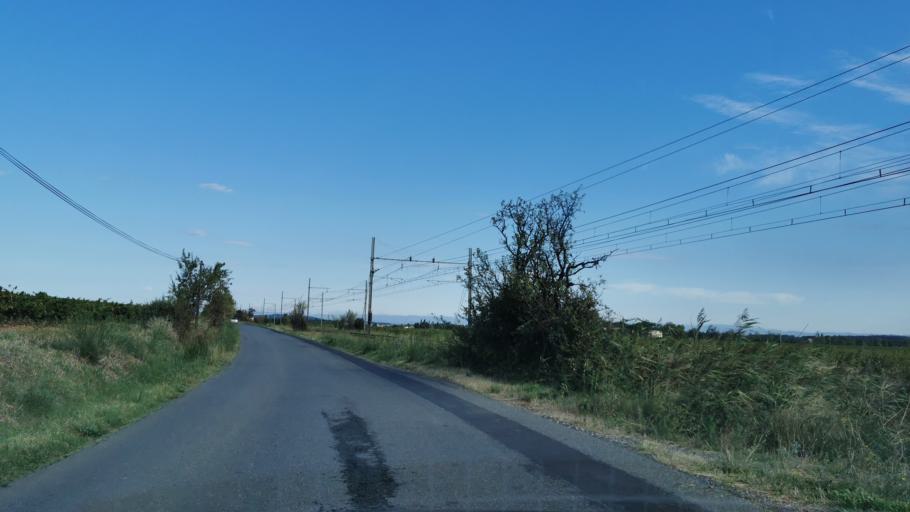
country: FR
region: Languedoc-Roussillon
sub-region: Departement de l'Aude
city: Narbonne
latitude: 43.1544
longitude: 3.0157
